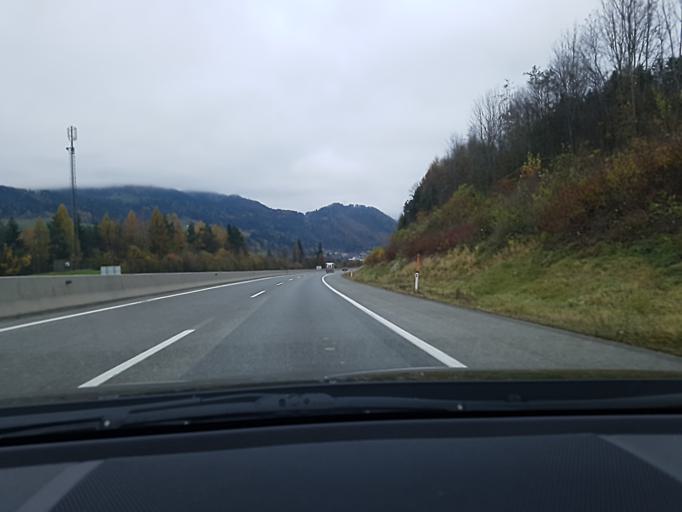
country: AT
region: Salzburg
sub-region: Politischer Bezirk Sankt Johann im Pongau
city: Pfarrwerfen
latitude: 47.4596
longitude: 13.2088
